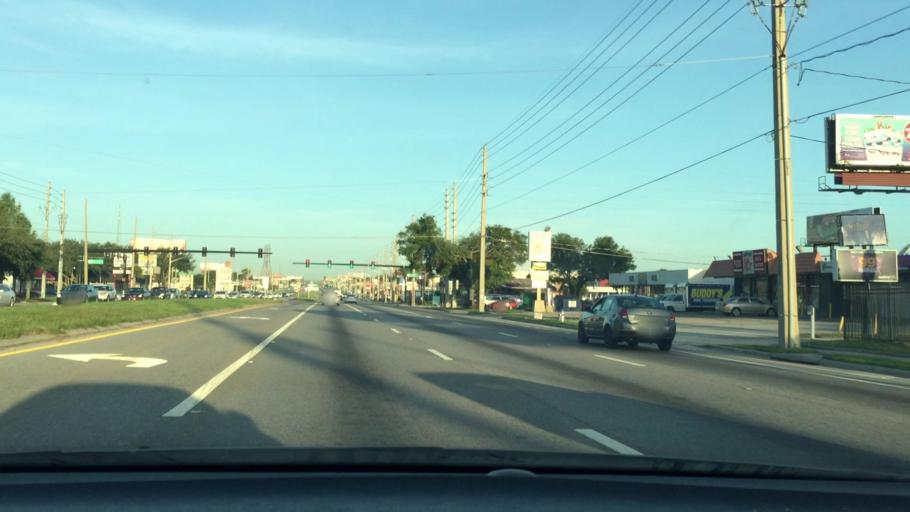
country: US
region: Florida
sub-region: Orange County
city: Pine Hills
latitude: 28.5526
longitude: -81.4462
